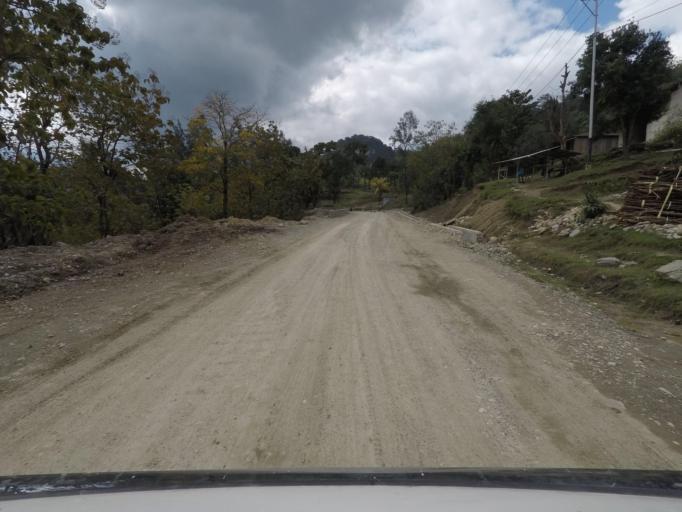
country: TL
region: Viqueque
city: Viqueque
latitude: -8.7907
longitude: 126.3760
